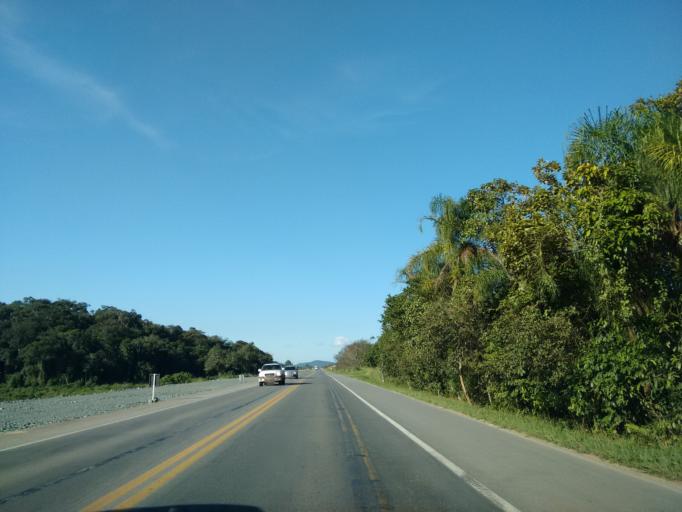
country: BR
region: Santa Catarina
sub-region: Guaramirim
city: Guaramirim
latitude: -26.4526
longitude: -48.9019
